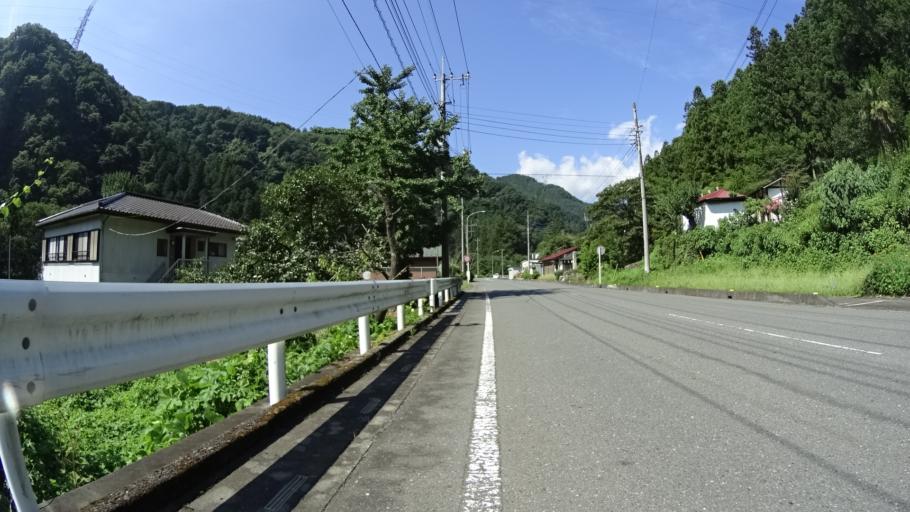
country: JP
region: Saitama
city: Chichibu
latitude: 36.0336
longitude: 138.9312
